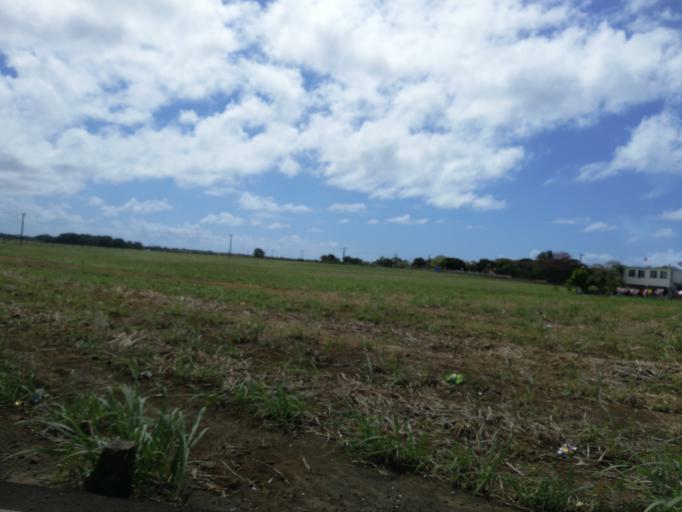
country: MU
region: Riviere du Rempart
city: Esperance Trebuchet
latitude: -20.0642
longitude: 57.6792
